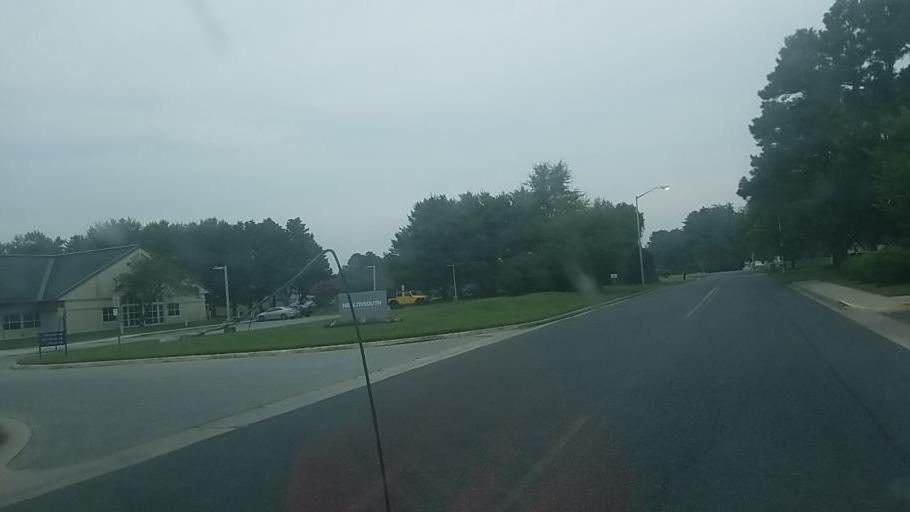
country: US
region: Maryland
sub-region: Wicomico County
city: Salisbury
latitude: 38.3691
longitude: -75.5475
